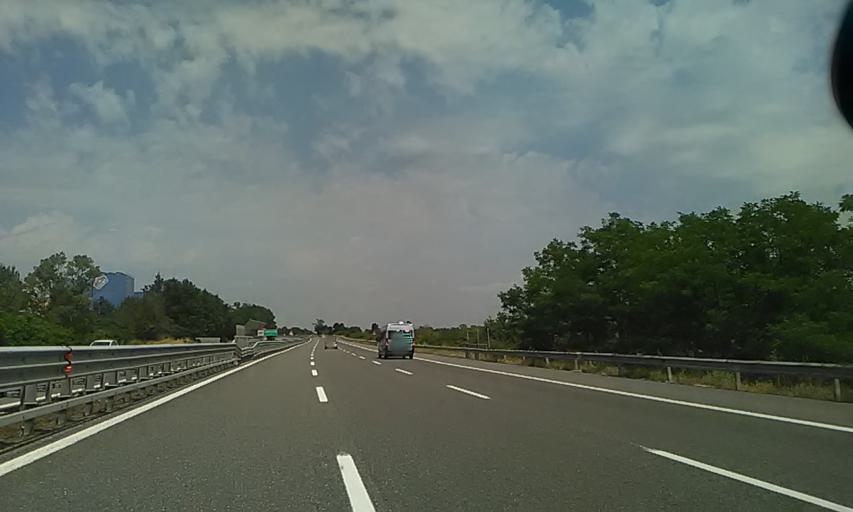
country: IT
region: Piedmont
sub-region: Provincia di Alessandria
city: Capriata d'Orba
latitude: 44.7169
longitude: 8.6668
